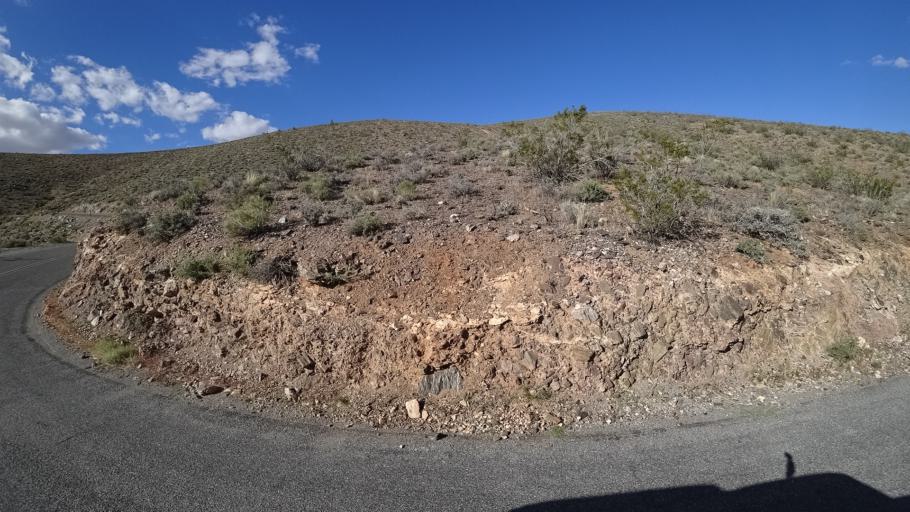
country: US
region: California
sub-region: San Bernardino County
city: Searles Valley
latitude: 36.3103
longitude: -117.1505
